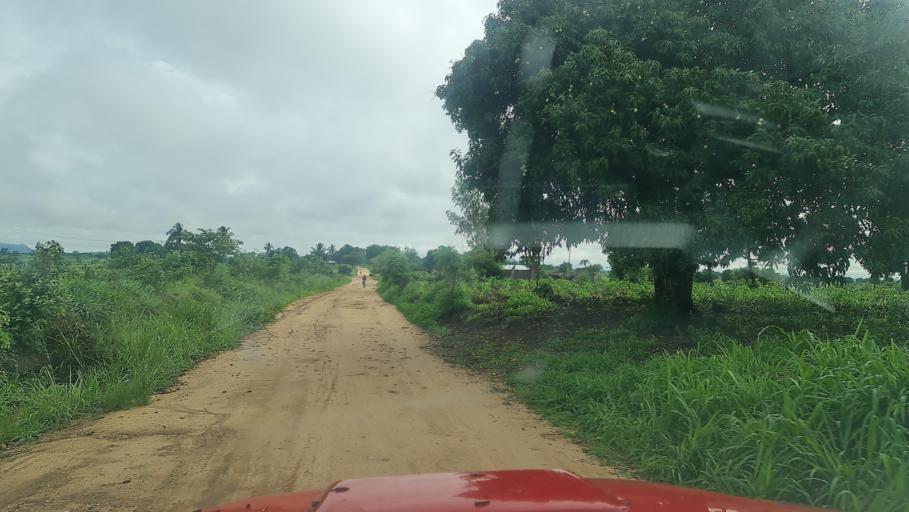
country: MW
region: Southern Region
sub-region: Nsanje District
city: Nsanje
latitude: -17.2926
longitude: 35.5986
